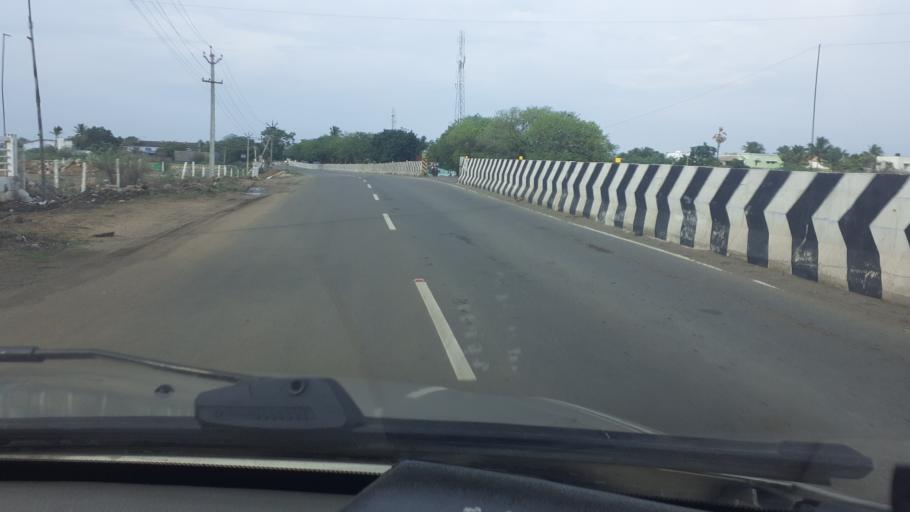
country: IN
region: Tamil Nadu
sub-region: Tirunelveli Kattabo
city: Tirunelveli
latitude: 8.6688
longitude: 77.7179
